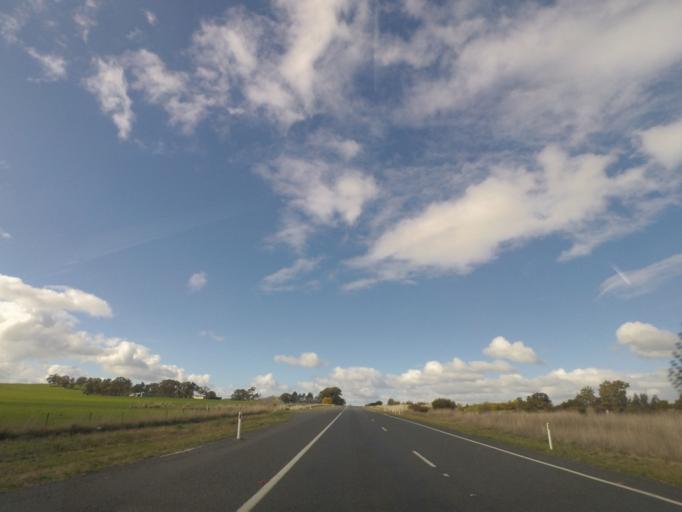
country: AU
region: New South Wales
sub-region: Greater Hume Shire
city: Jindera
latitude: -35.9241
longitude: 147.0489
